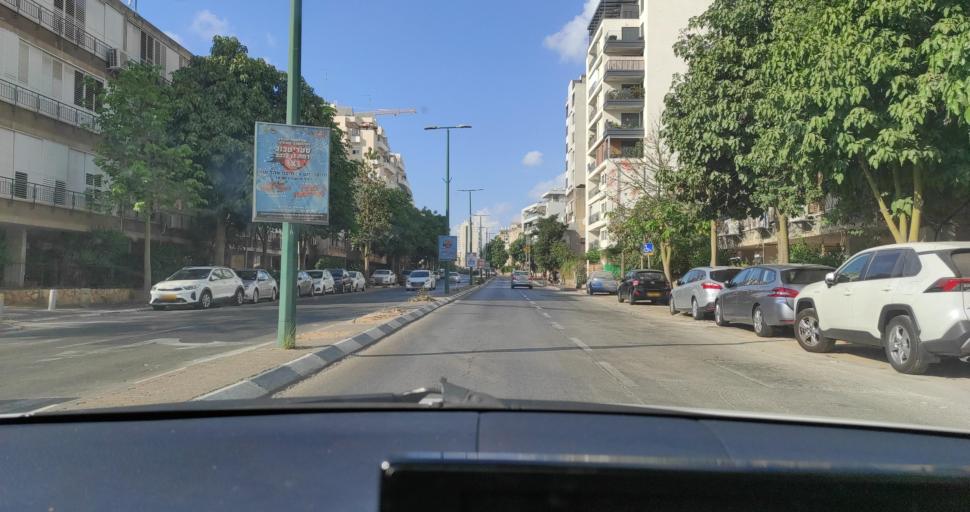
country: IL
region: Tel Aviv
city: Giv`atayim
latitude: 32.0622
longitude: 34.8284
